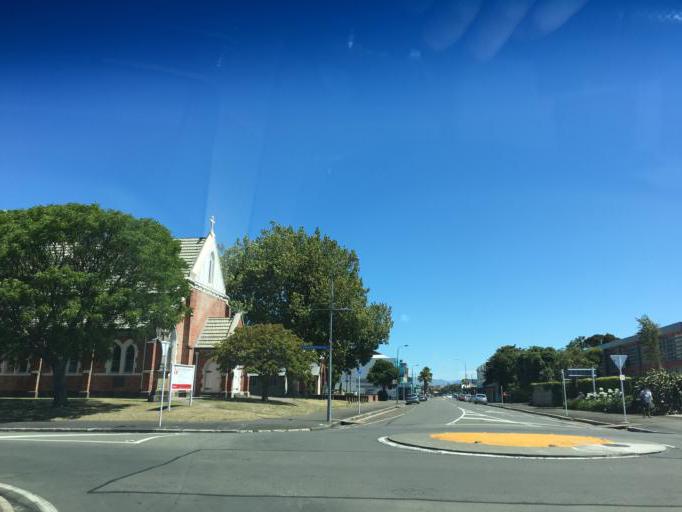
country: NZ
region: Gisborne
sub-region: Gisborne District
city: Gisborne
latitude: -38.6628
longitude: 178.0243
